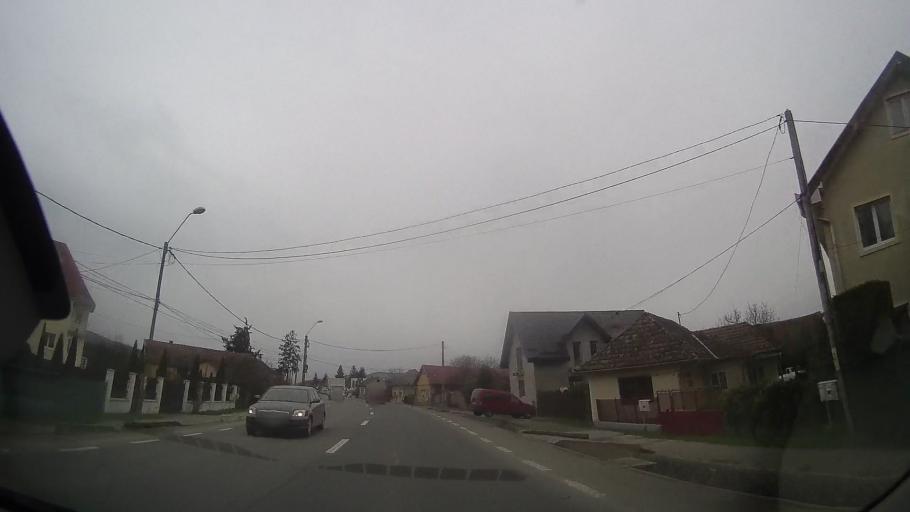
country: RO
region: Mures
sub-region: Comuna Santana de Mures
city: Santana de Mures
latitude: 46.5764
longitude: 24.5543
